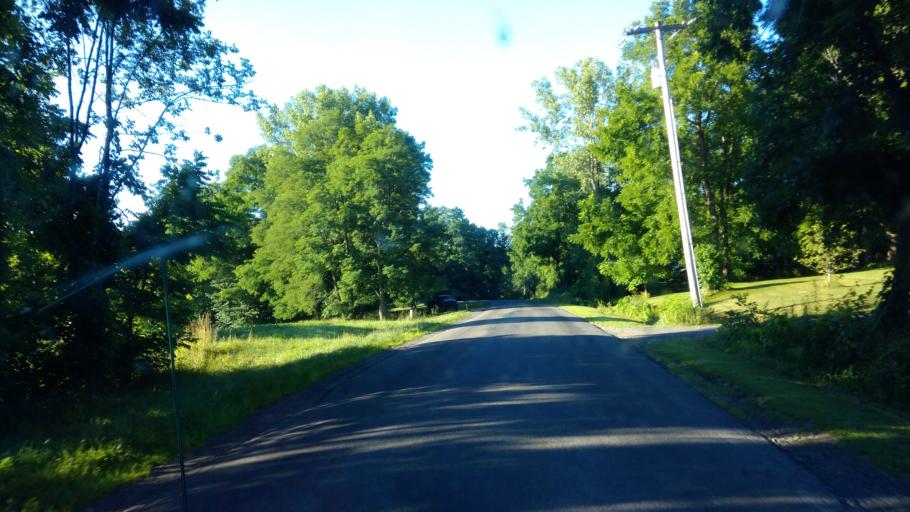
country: US
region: New York
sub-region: Wayne County
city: Lyons
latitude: 43.1182
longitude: -77.0385
